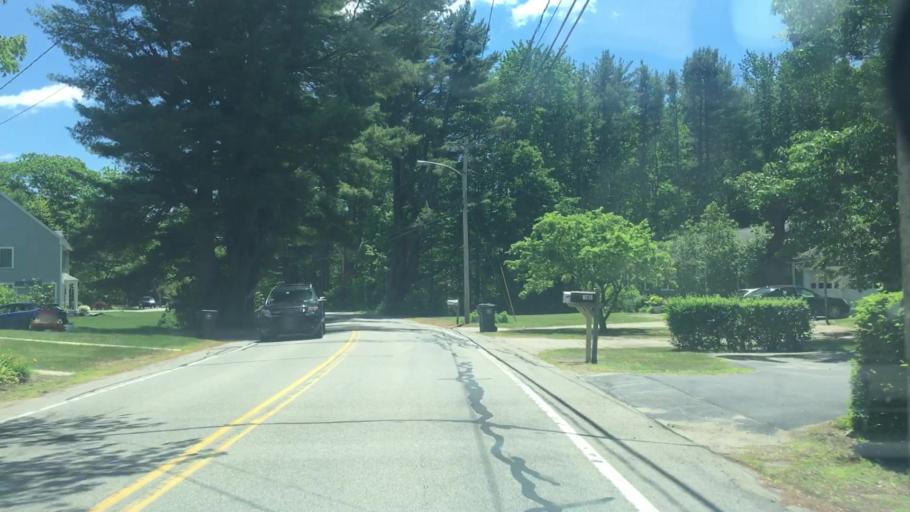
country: US
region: Maine
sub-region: York County
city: Kennebunk
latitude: 43.3675
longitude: -70.5238
